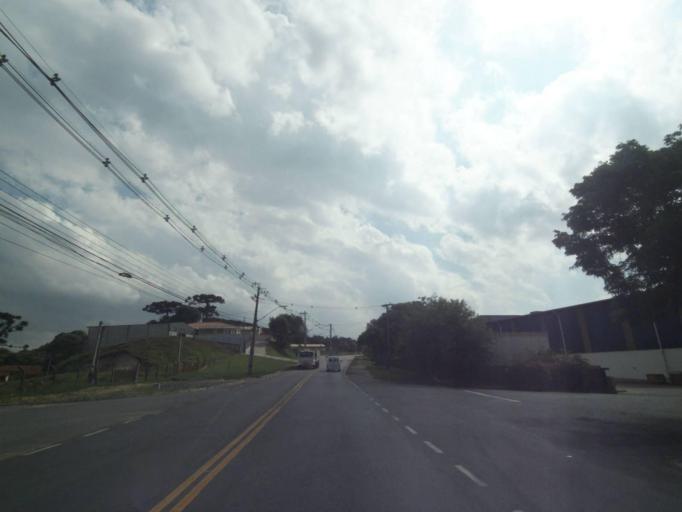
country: BR
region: Parana
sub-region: Araucaria
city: Araucaria
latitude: -25.5158
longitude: -49.3397
